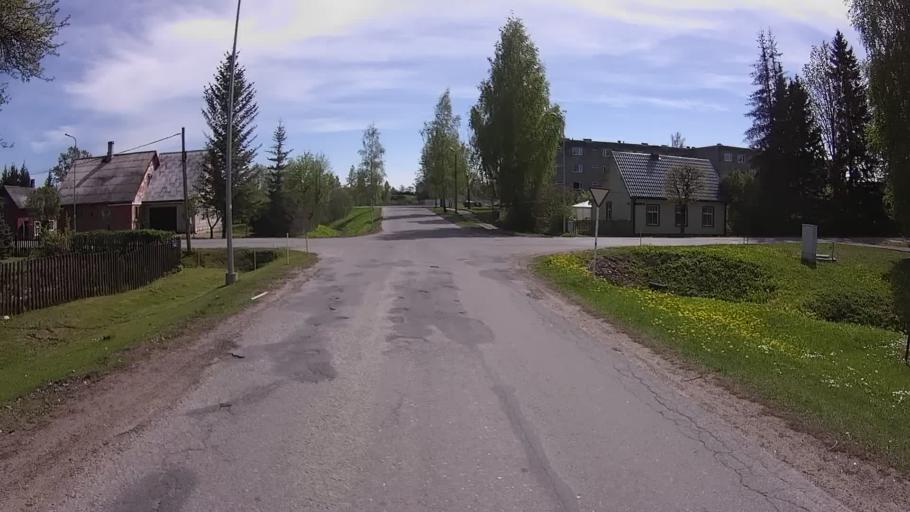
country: EE
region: Valgamaa
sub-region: Valga linn
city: Valga
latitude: 57.7791
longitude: 26.0634
